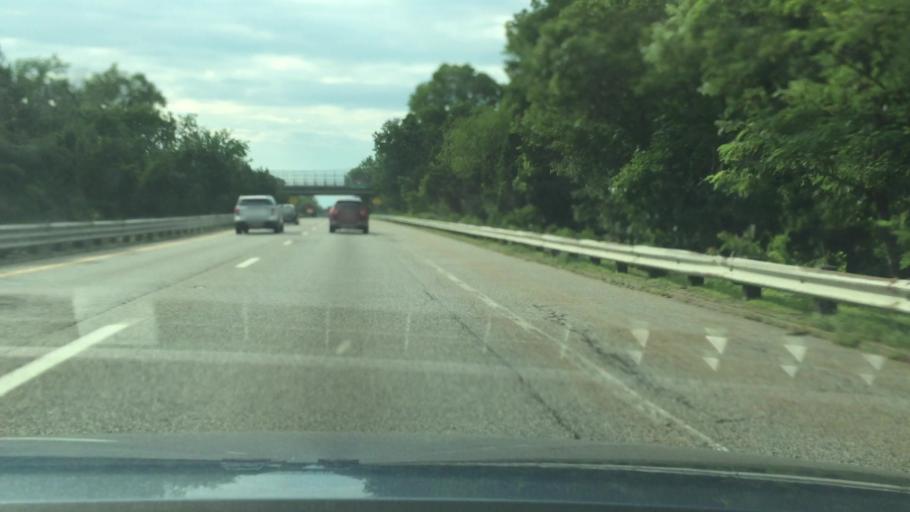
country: US
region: Massachusetts
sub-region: Plymouth County
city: Hanover
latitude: 42.1447
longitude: -70.8323
